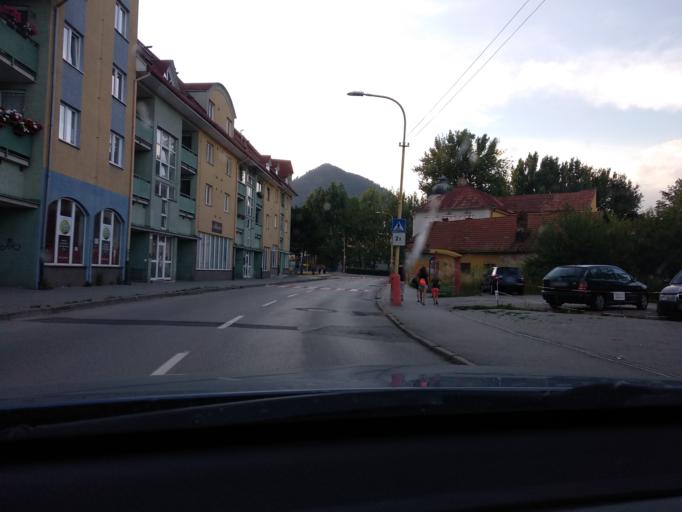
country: SK
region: Zilinsky
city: Ruzomberok
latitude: 49.0782
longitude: 19.3068
